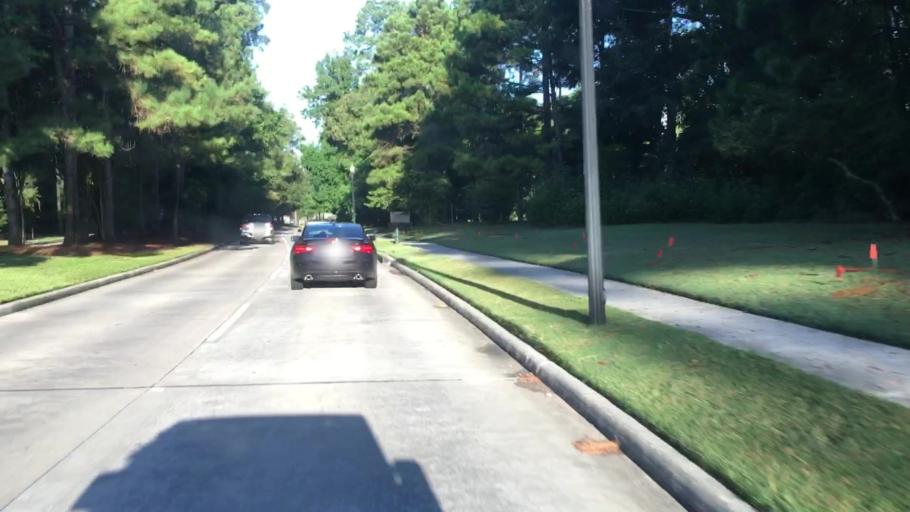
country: US
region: Texas
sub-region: Harris County
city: Atascocita
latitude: 29.9790
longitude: -95.1885
